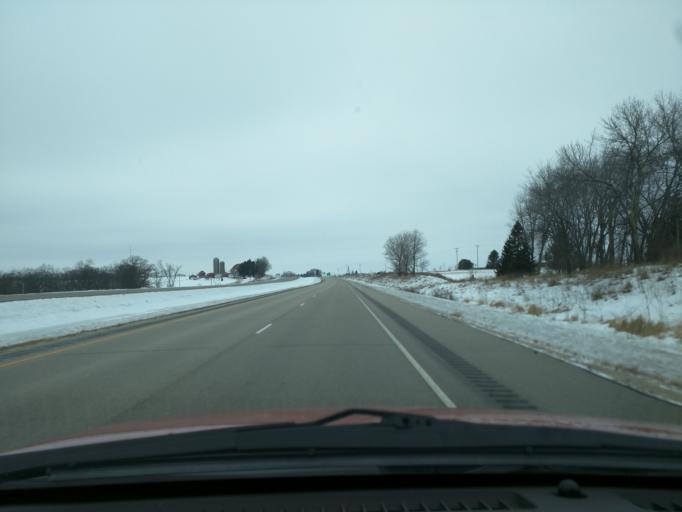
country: US
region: Wisconsin
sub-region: Trempealeau County
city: Trempealeau
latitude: 43.9117
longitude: -91.5655
